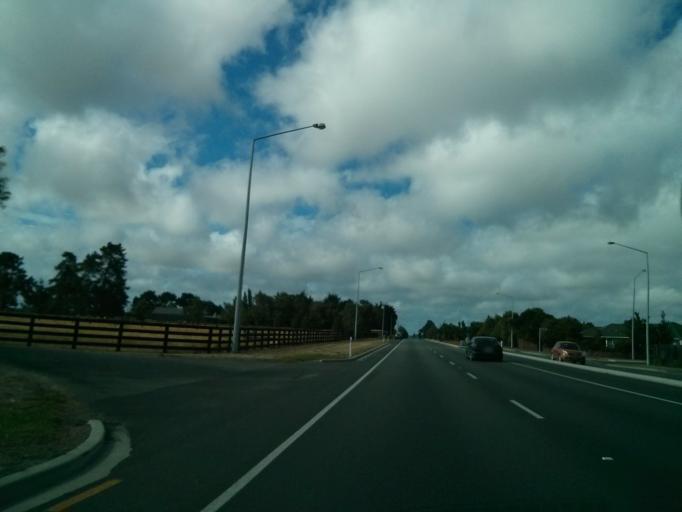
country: NZ
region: Canterbury
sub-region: Selwyn District
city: Prebbleton
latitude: -43.5180
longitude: 172.5354
